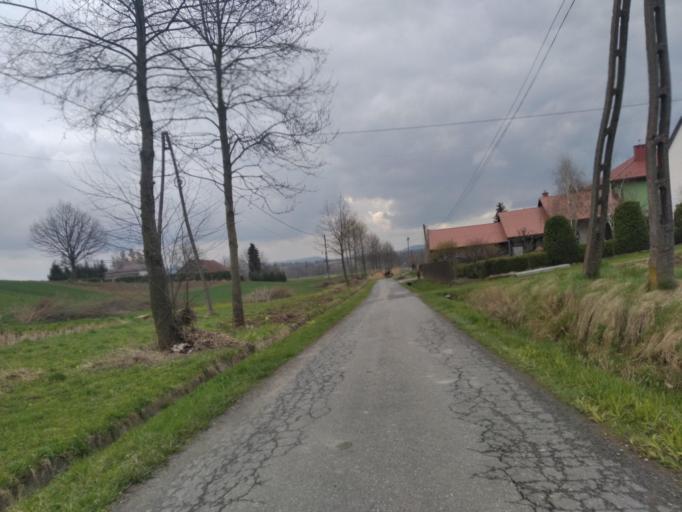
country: PL
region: Subcarpathian Voivodeship
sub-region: Powiat strzyzowski
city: Wisniowa
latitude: 49.8784
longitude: 21.7060
